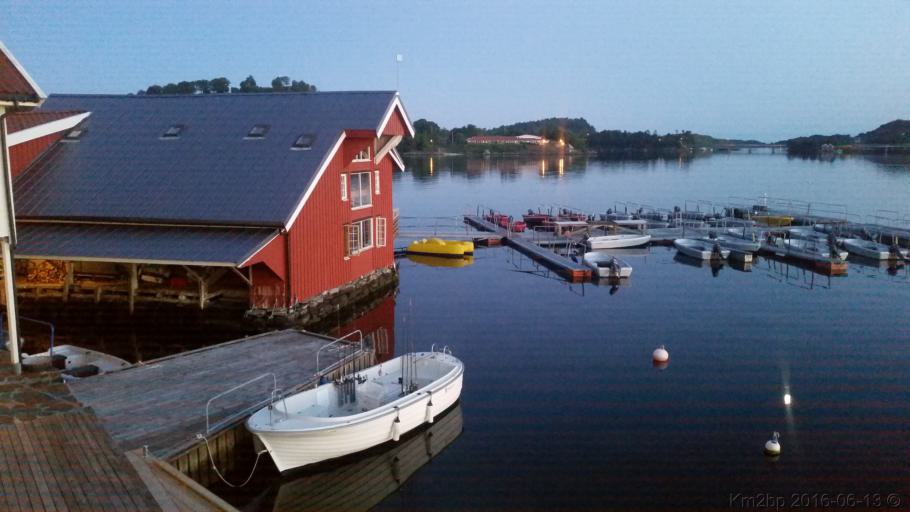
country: NO
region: Rogaland
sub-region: Finnoy
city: Judaberg
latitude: 59.2597
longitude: 5.8475
